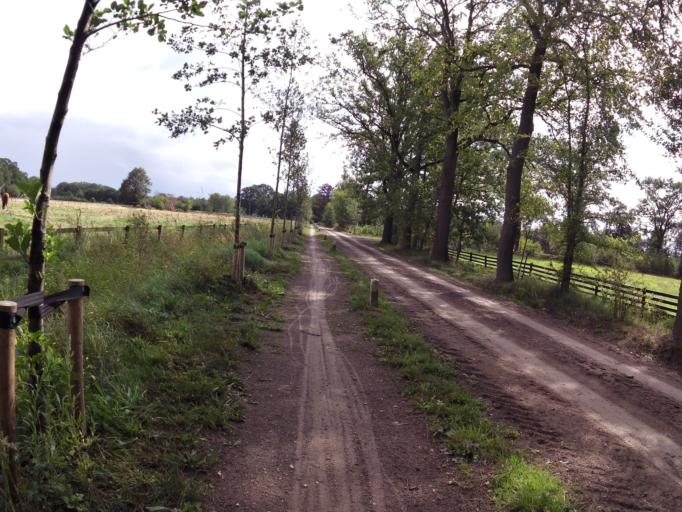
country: NL
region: Gelderland
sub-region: Gemeente Winterswijk
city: Winterswijk
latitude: 51.9888
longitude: 6.6697
